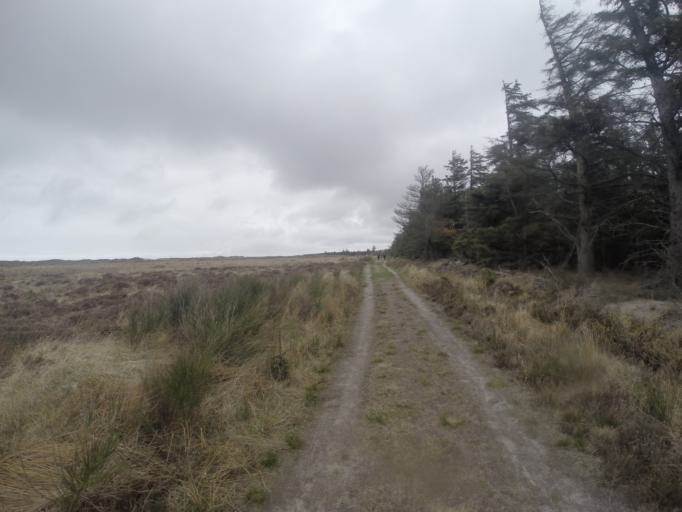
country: DK
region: North Denmark
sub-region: Thisted Kommune
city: Hurup
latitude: 56.9059
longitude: 8.3449
